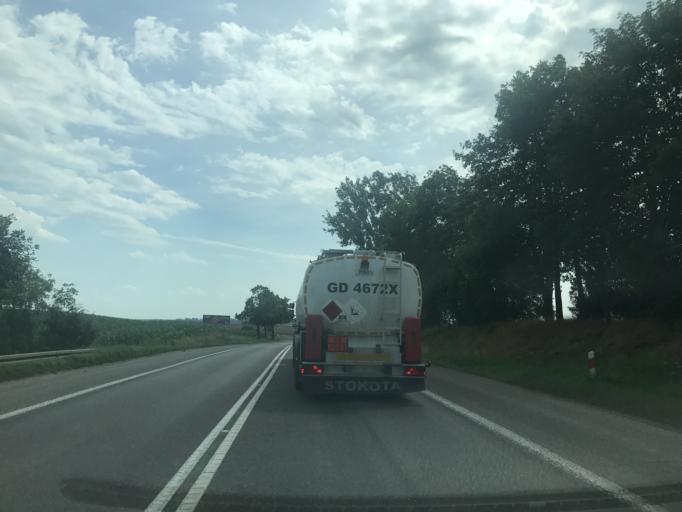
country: PL
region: Warmian-Masurian Voivodeship
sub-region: Powiat ostrodzki
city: Ostroda
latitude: 53.6562
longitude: 20.0507
